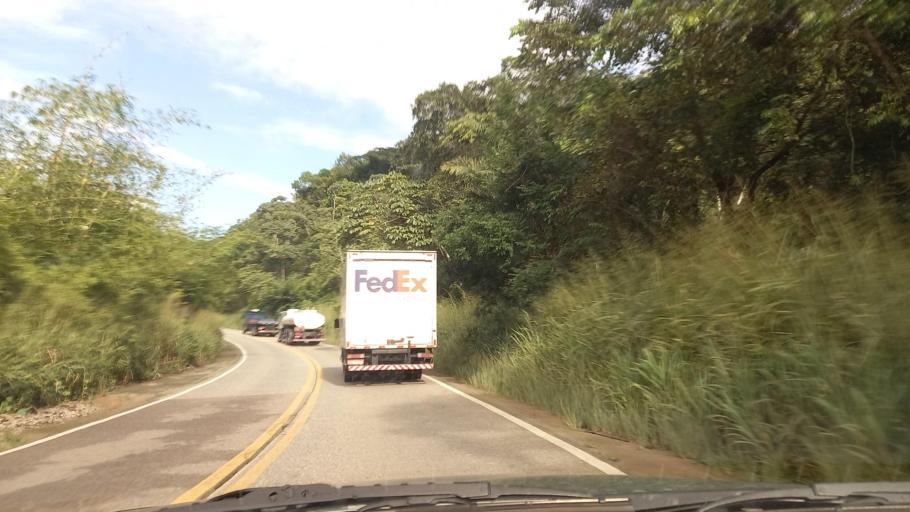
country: BR
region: Pernambuco
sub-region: Catende
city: Catende
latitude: -8.6910
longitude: -35.6701
